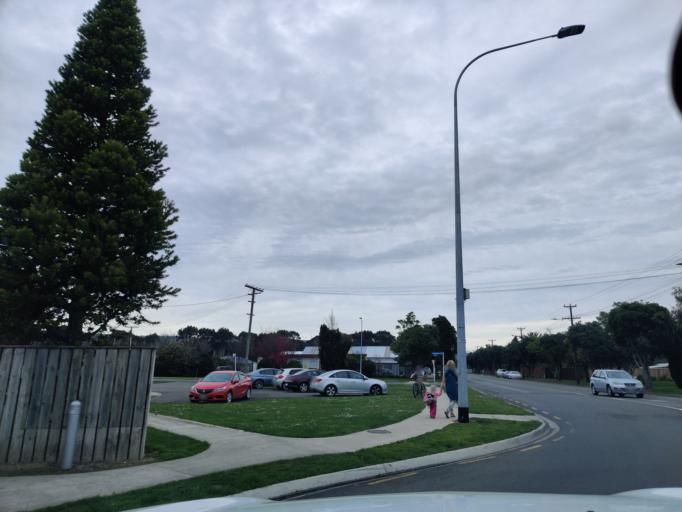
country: NZ
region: Manawatu-Wanganui
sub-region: Palmerston North City
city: Palmerston North
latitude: -40.2931
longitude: 175.7547
